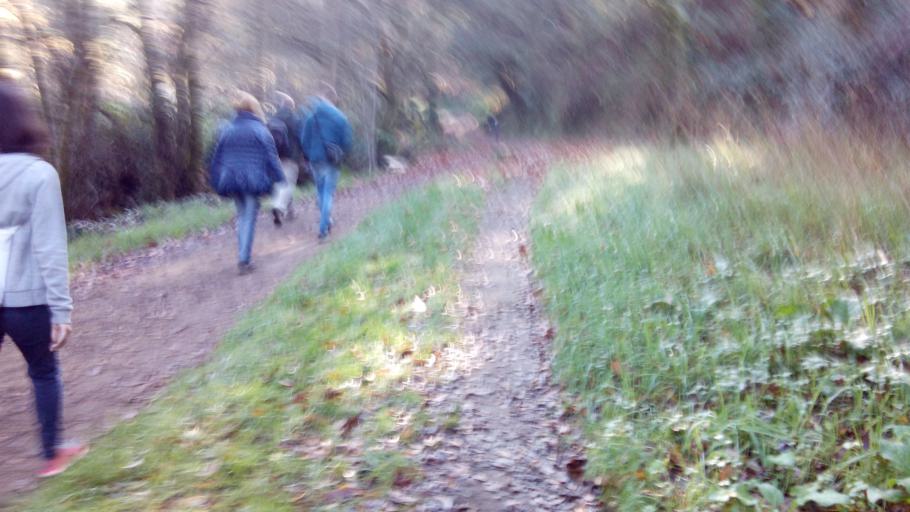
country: ES
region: Galicia
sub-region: Provincia de Pontevedra
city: Meis
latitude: 42.4829
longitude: -8.7424
